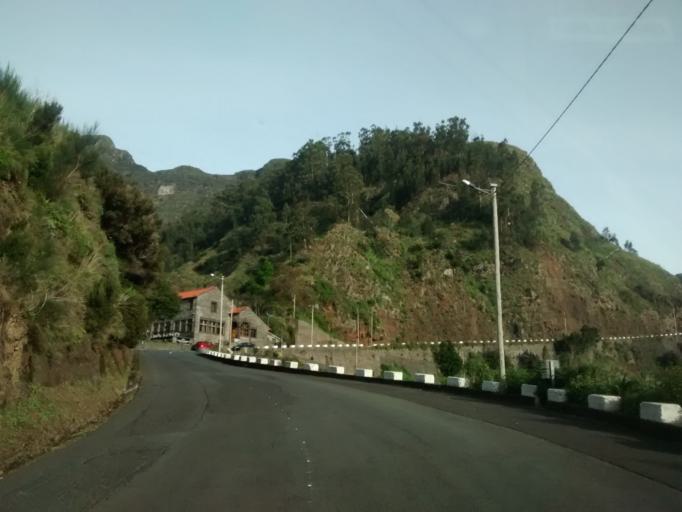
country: PT
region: Madeira
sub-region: Camara de Lobos
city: Curral das Freiras
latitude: 32.7355
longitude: -17.0251
